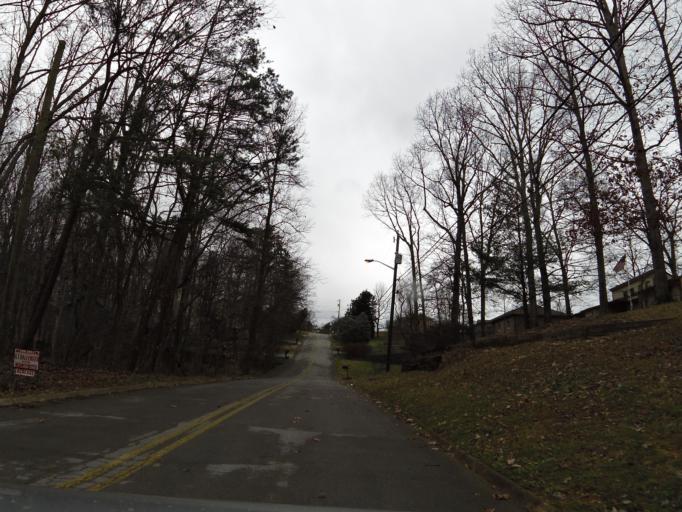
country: US
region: Tennessee
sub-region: Knox County
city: Knoxville
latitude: 35.9890
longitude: -84.0328
